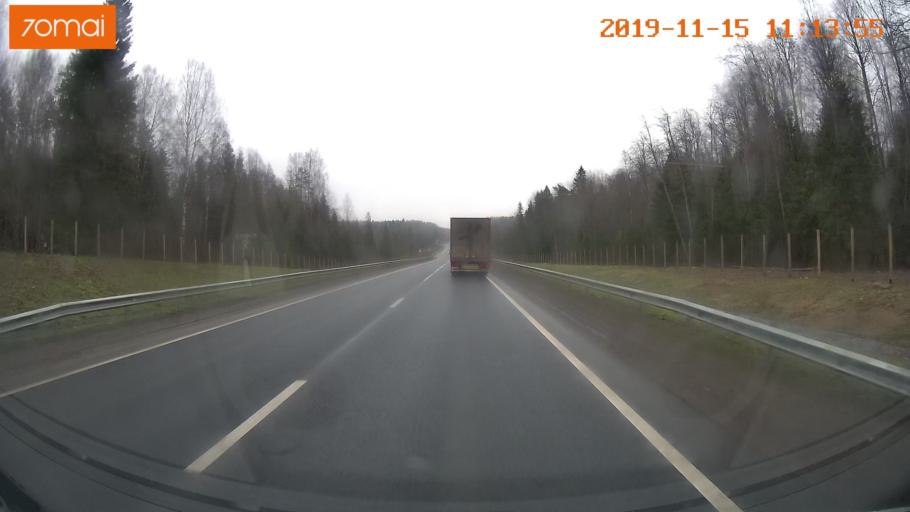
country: RU
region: Vologda
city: Chebsara
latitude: 59.1234
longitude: 39.1775
